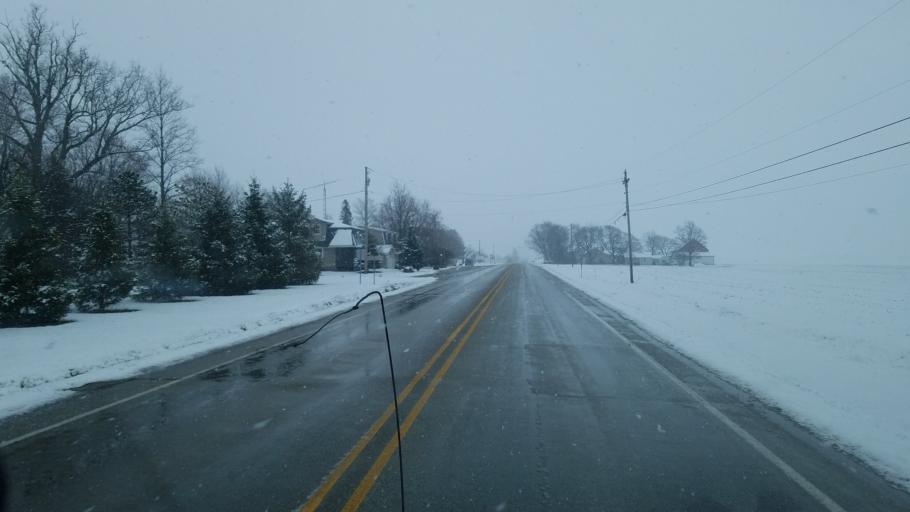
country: US
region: Indiana
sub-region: Wayne County
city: Hagerstown
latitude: 39.9754
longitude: -85.0834
